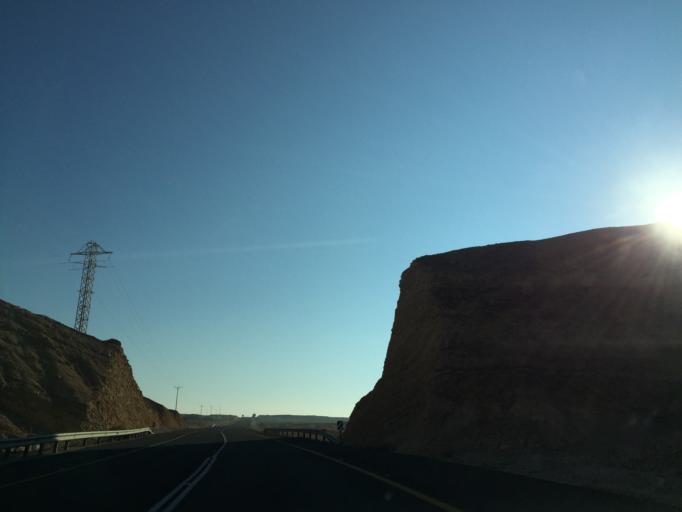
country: IL
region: Southern District
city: Mitzpe Ramon
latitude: 30.2782
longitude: 35.0069
